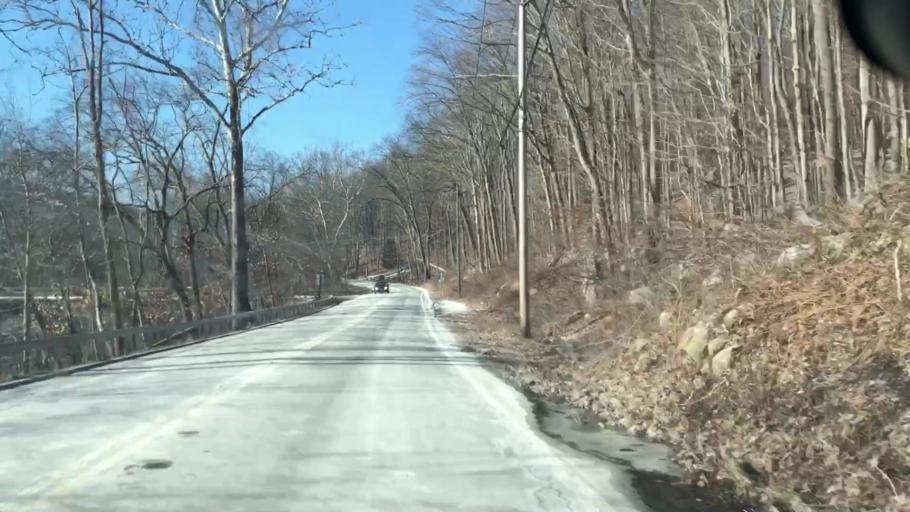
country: US
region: New York
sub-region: Putnam County
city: Carmel Hamlet
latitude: 41.3886
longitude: -73.6778
